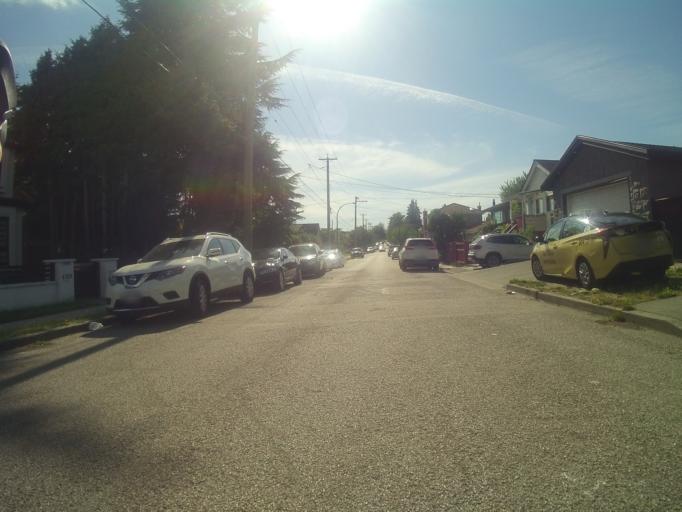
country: CA
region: British Columbia
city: Vancouver
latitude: 49.2167
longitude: -123.0965
